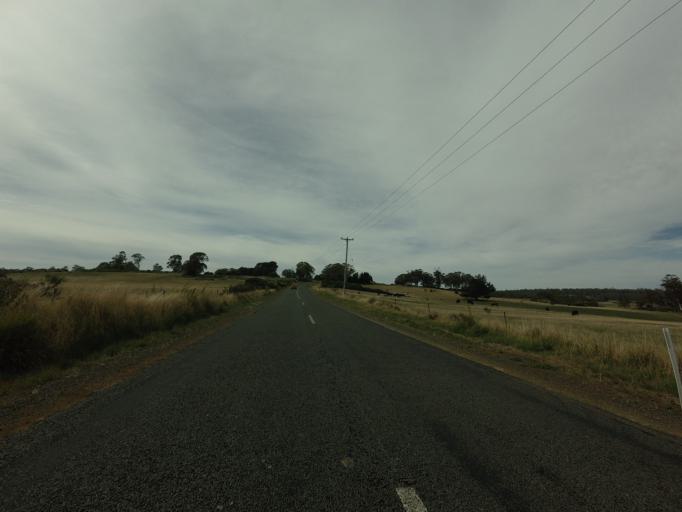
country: AU
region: Tasmania
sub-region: Brighton
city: Bridgewater
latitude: -42.3929
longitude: 147.4318
